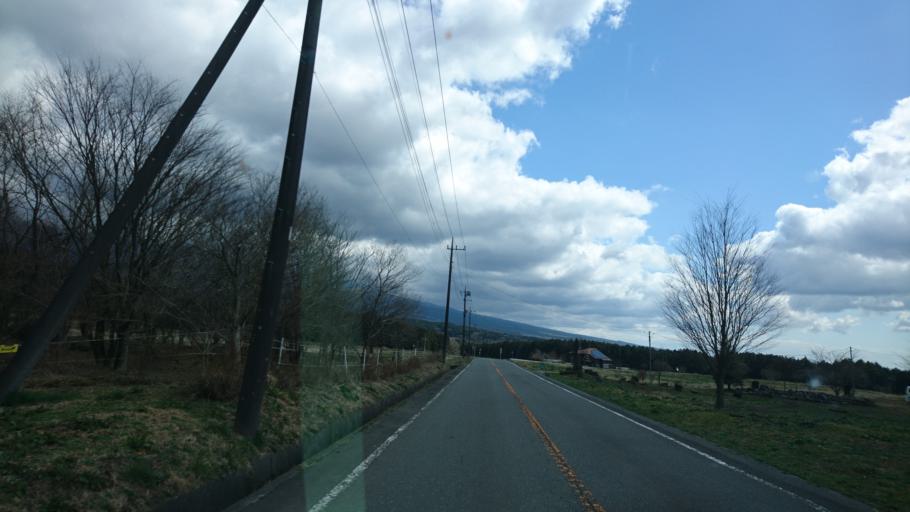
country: JP
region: Yamanashi
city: Fujikawaguchiko
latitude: 35.3757
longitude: 138.6011
